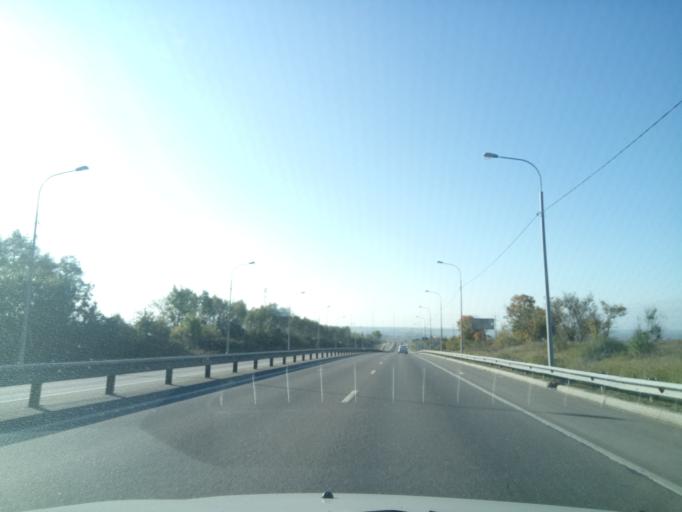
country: RU
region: Nizjnij Novgorod
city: Burevestnik
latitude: 56.1998
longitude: 43.9248
